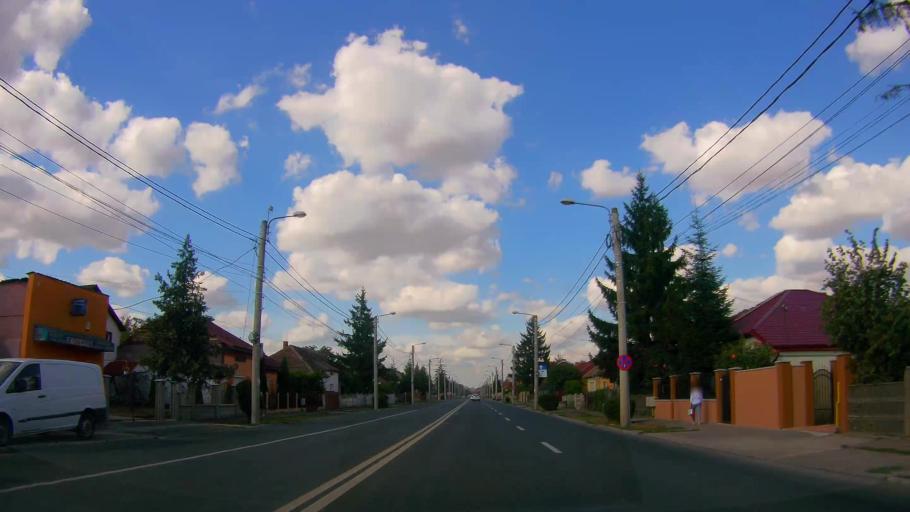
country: RO
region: Satu Mare
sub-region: Municipiul Satu Mare
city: Satu Mare
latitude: 47.7633
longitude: 22.8835
